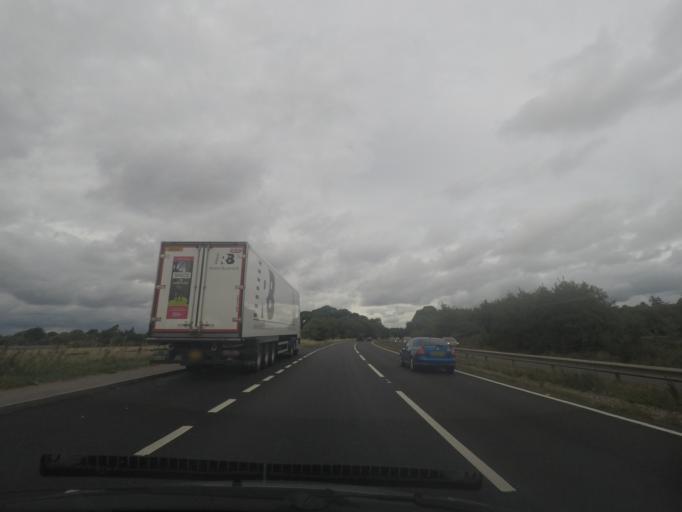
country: GB
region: England
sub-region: West Berkshire
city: Hermitage
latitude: 51.4790
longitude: -1.3025
